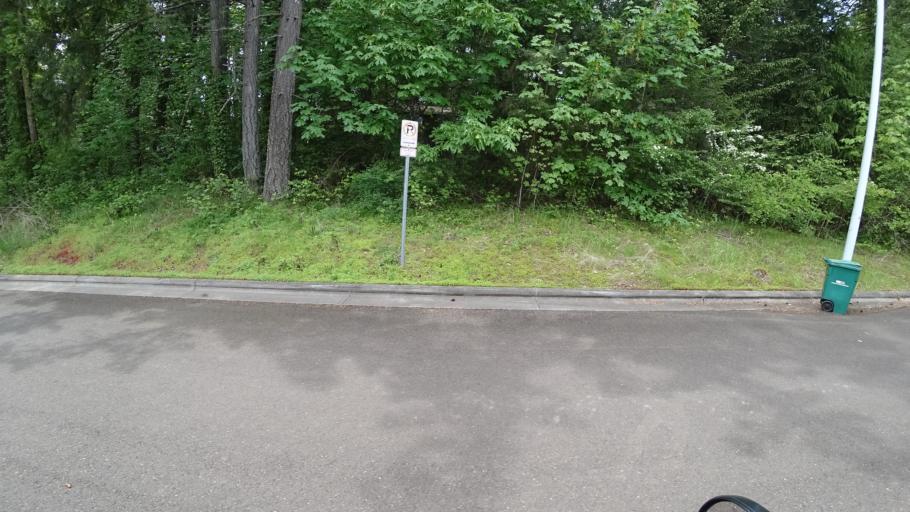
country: US
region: Oregon
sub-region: Washington County
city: Aloha
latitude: 45.4625
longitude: -122.8586
